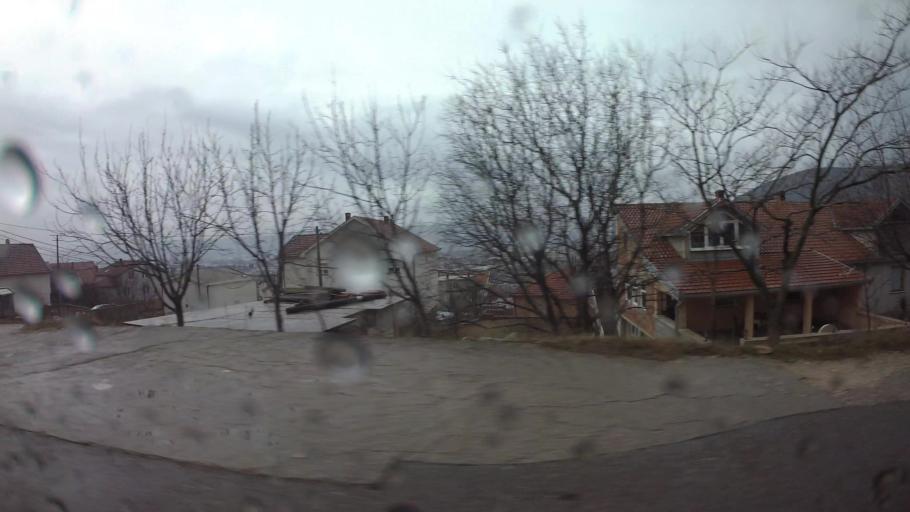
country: BA
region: Federation of Bosnia and Herzegovina
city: Rodoc
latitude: 43.3154
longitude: 17.8369
